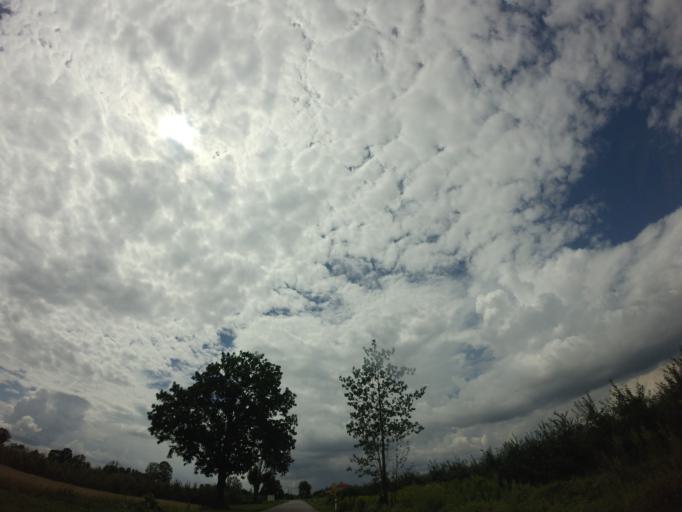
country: PL
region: Lublin Voivodeship
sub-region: Powiat opolski
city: Wilkow
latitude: 51.2402
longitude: 21.8496
